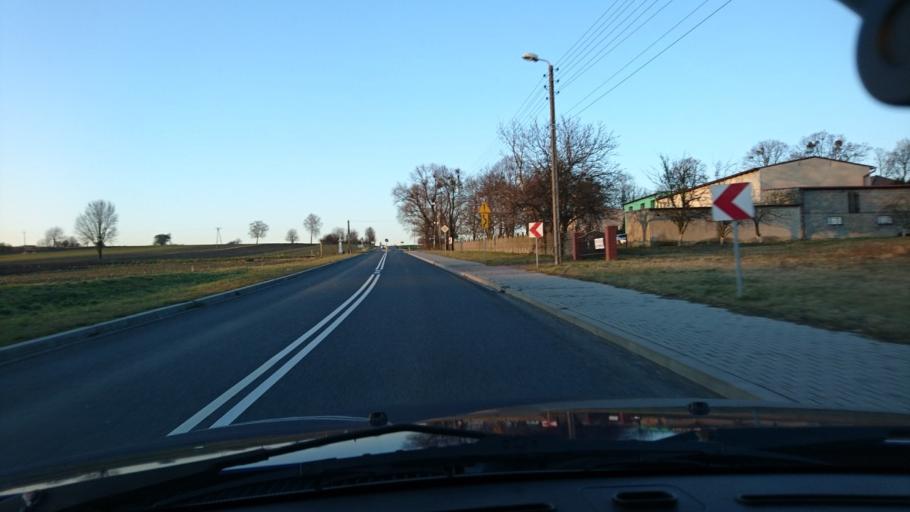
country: PL
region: Silesian Voivodeship
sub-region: Powiat gliwicki
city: Wielowies
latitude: 50.4773
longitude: 18.6087
